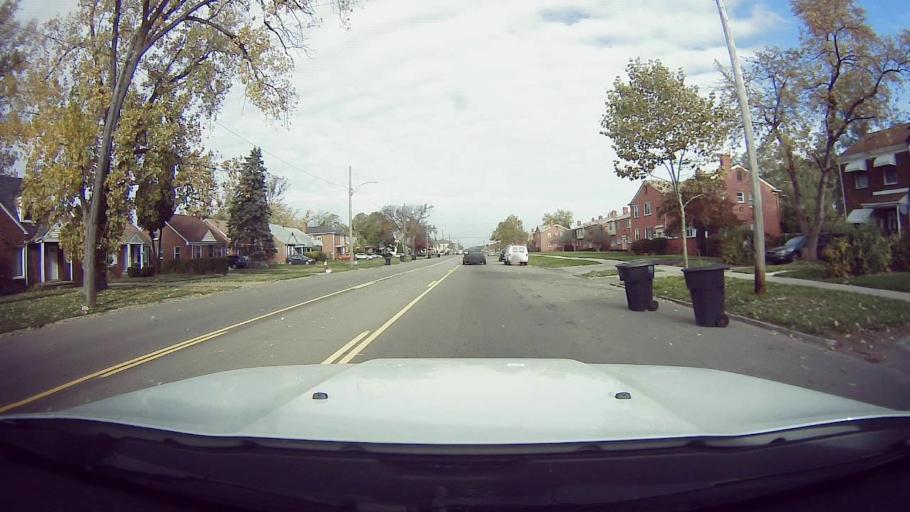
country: US
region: Michigan
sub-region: Oakland County
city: Oak Park
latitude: 42.4415
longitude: -83.1808
